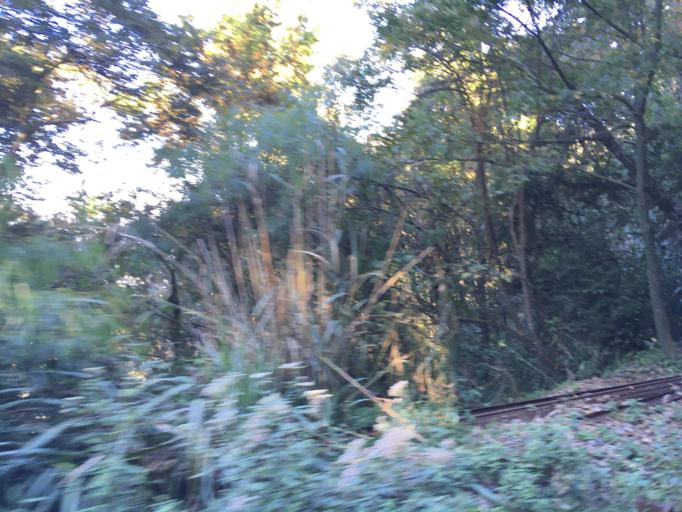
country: TW
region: Taiwan
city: Lugu
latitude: 23.5172
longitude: 120.8066
